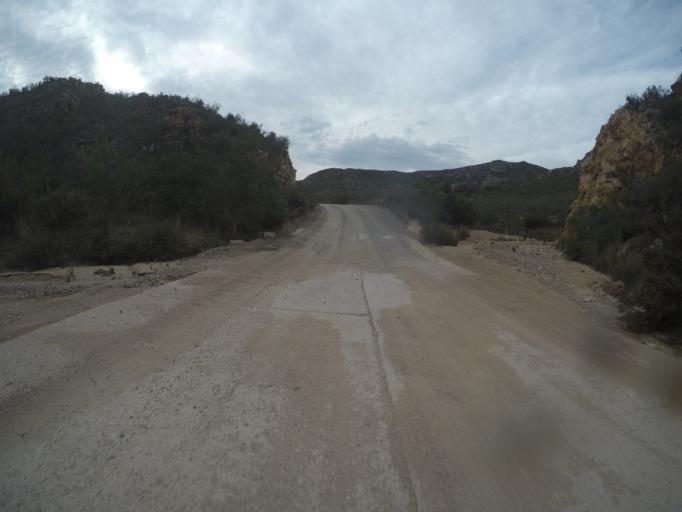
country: ZA
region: Eastern Cape
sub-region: Cacadu District Municipality
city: Willowmore
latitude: -33.5096
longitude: 23.6370
